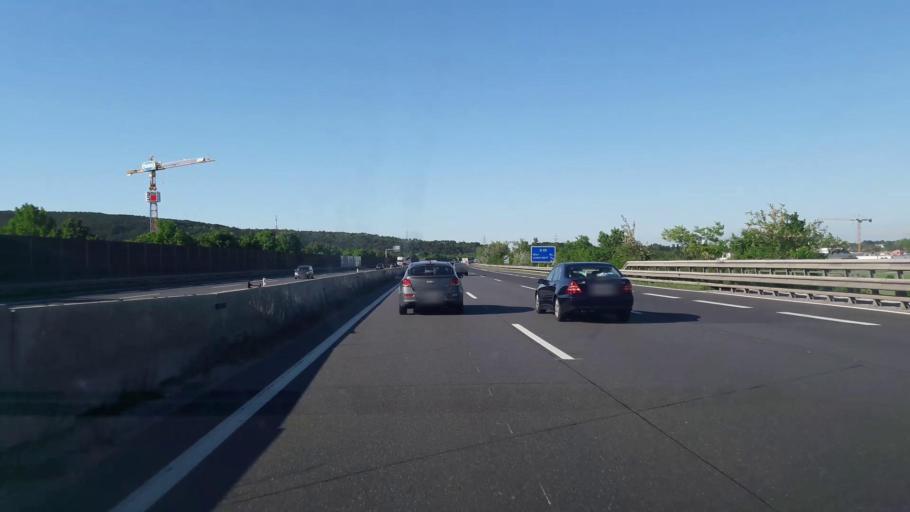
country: AT
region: Lower Austria
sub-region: Politischer Bezirk Wiener Neustadt
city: Theresienfeld
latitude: 47.8603
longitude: 16.1864
